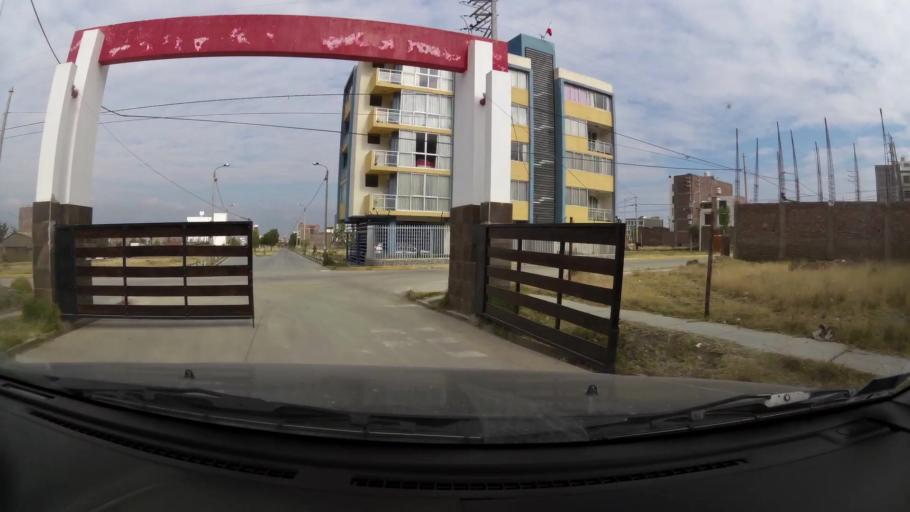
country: PE
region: Junin
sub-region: Provincia de Huancayo
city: Huancayo
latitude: -12.0497
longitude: -75.1885
